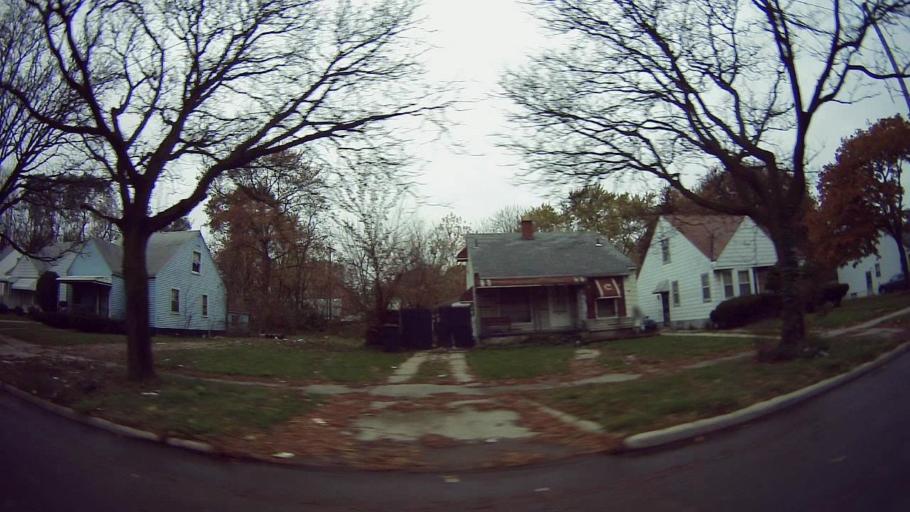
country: US
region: Michigan
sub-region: Wayne County
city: Dearborn Heights
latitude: 42.3756
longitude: -83.2364
